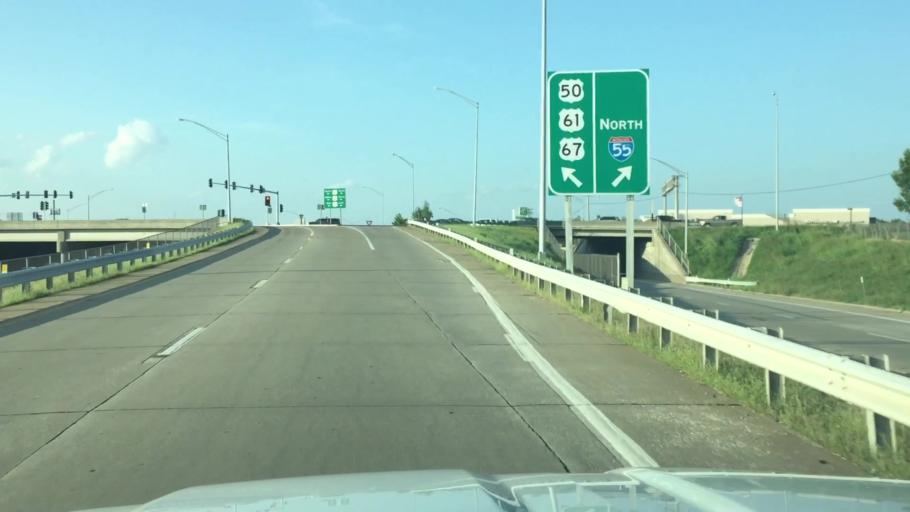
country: US
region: Missouri
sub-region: Saint Louis County
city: Mehlville
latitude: 38.5100
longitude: -90.3359
